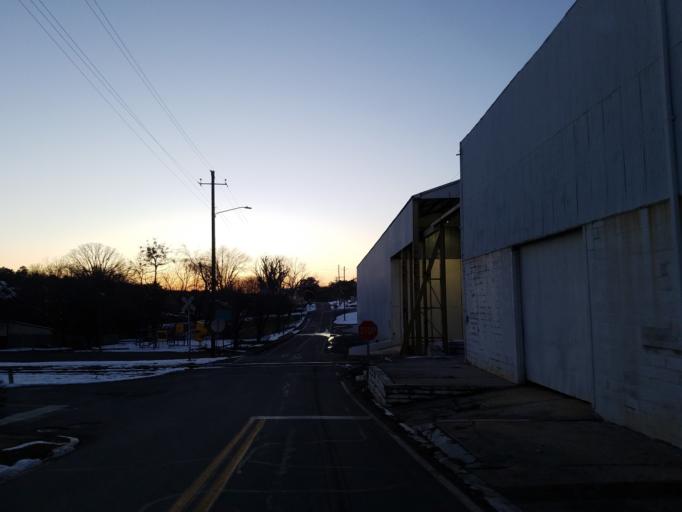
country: US
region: Georgia
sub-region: Pickens County
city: Nelson
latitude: 34.3821
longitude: -84.3709
